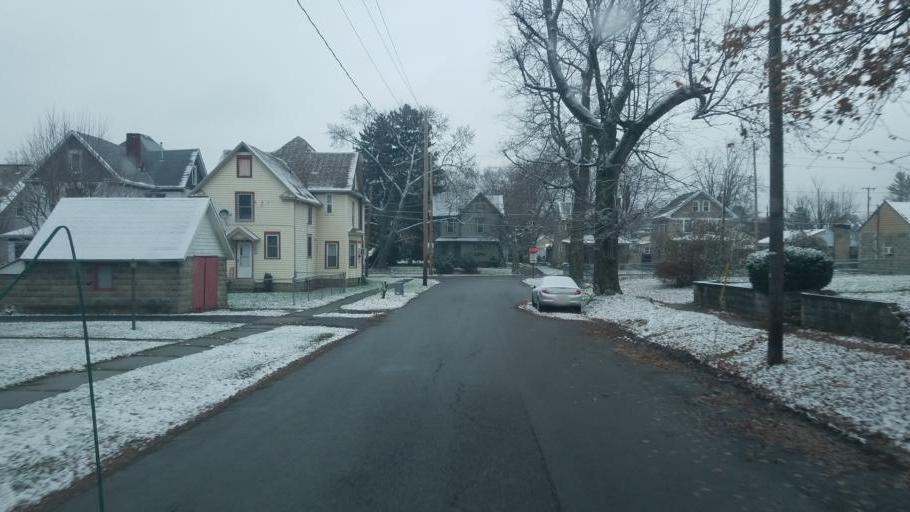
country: US
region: Ohio
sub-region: Marion County
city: Marion
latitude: 40.5836
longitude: -83.1248
